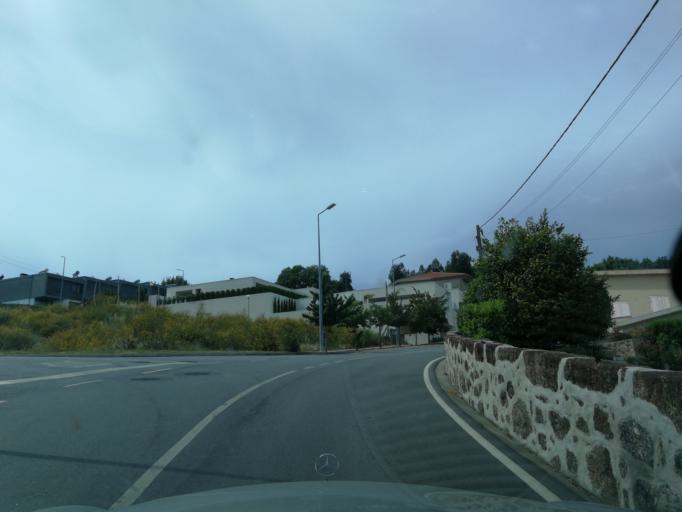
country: PT
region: Braga
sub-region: Vila Nova de Famalicao
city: Calendario
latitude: 41.4079
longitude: -8.5328
